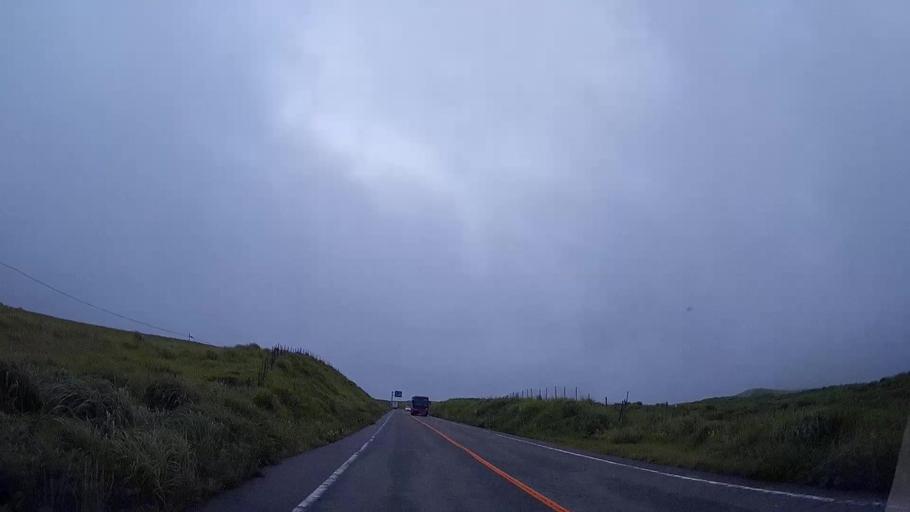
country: JP
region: Kumamoto
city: Aso
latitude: 33.0043
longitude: 131.0702
